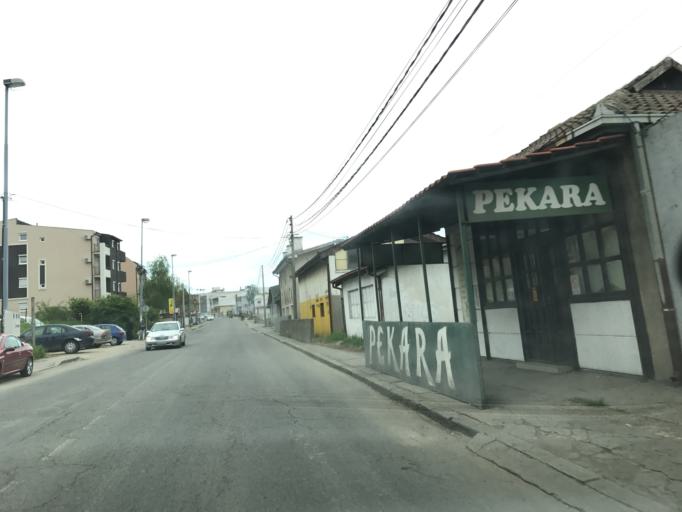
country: RS
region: Central Serbia
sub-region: Belgrade
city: Palilula
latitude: 44.7976
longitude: 20.5218
